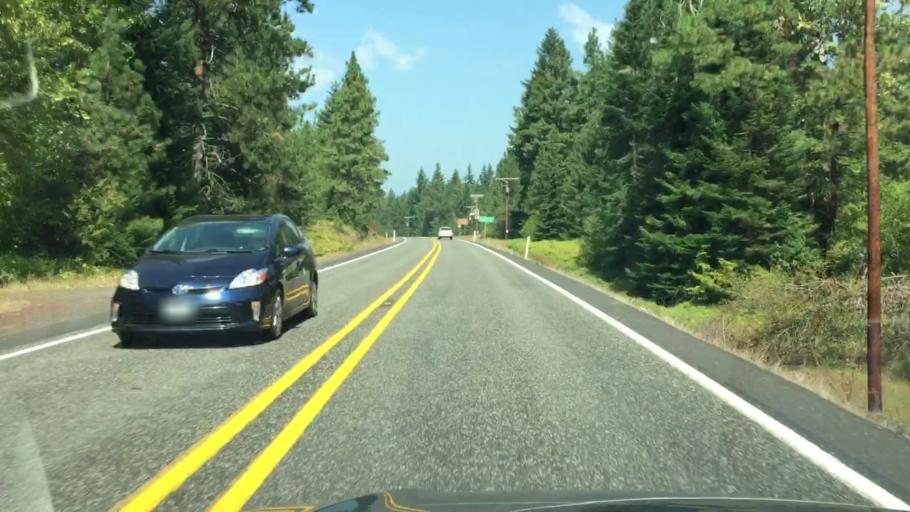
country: US
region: Washington
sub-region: Klickitat County
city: White Salmon
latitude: 45.9619
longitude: -121.4895
